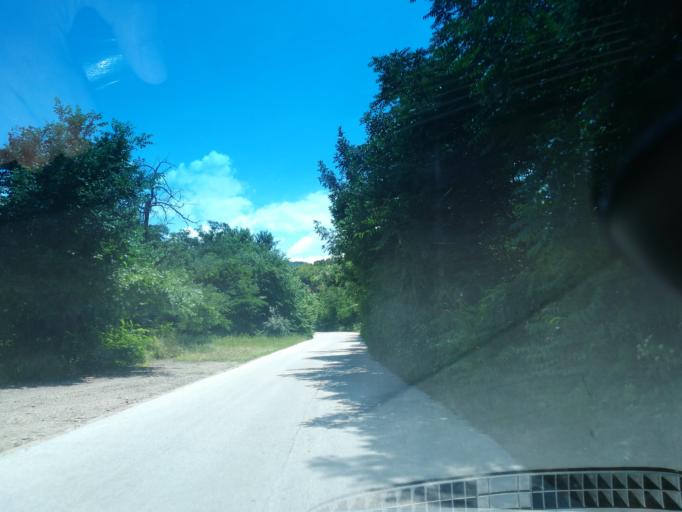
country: BG
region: Khaskovo
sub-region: Obshtina Mineralni Bani
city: Mineralni Bani
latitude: 41.9821
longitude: 25.2450
